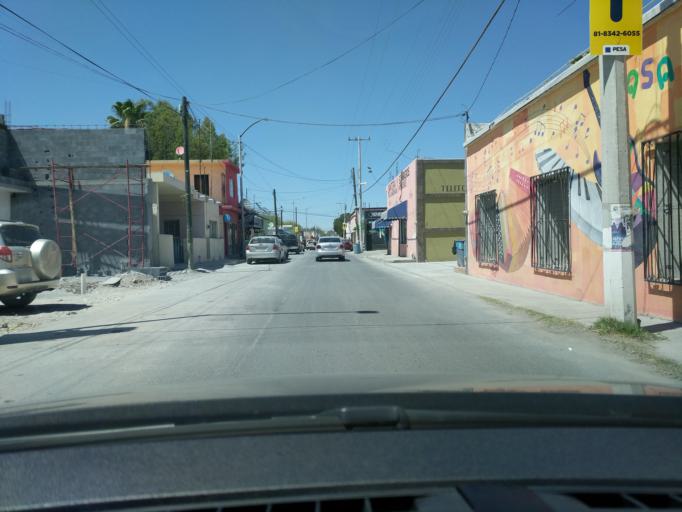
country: MX
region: Nuevo Leon
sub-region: Salinas Victoria
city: Las Torres
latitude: 25.9613
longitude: -100.2917
